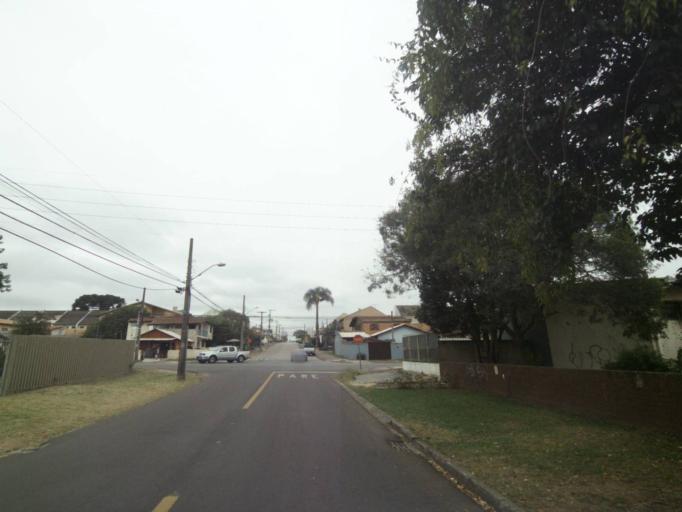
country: BR
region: Parana
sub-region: Pinhais
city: Pinhais
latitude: -25.4758
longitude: -49.2322
